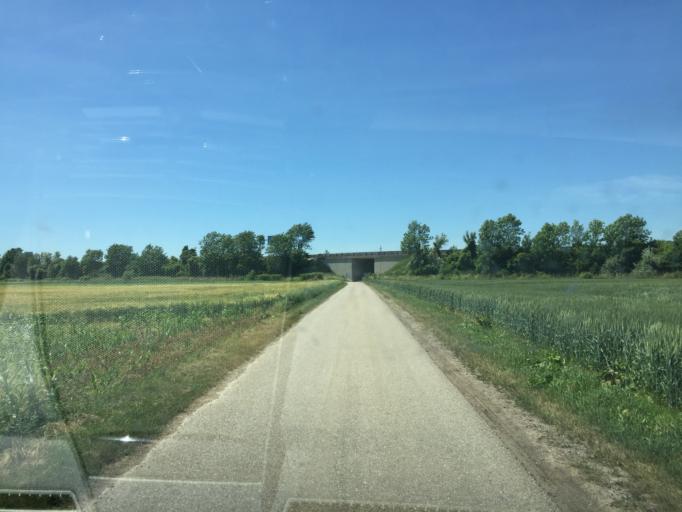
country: AT
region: Lower Austria
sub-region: Politischer Bezirk Sankt Polten
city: Herzogenburg
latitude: 48.2358
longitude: 15.6844
